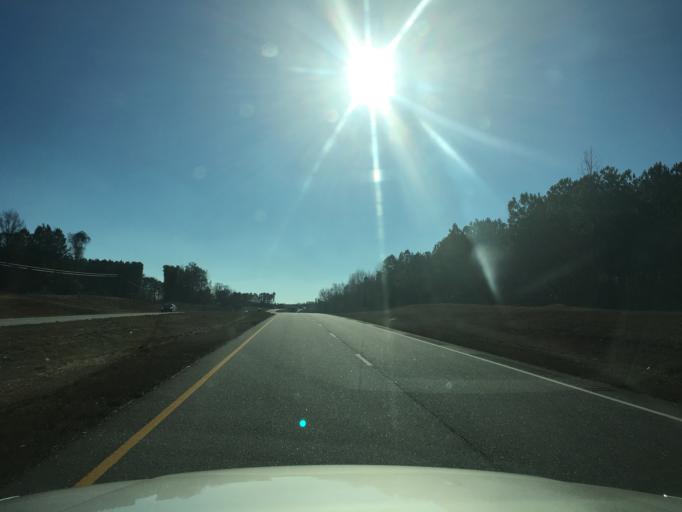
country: US
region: Georgia
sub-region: Carroll County
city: Carrollton
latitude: 33.4939
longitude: -85.0876
